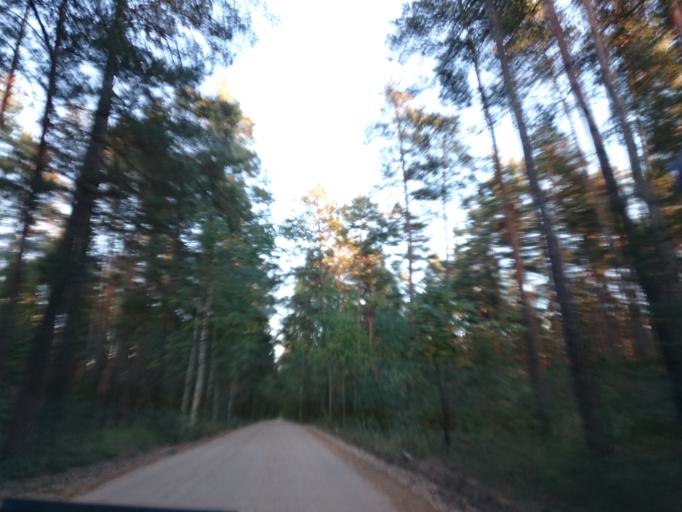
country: LV
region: Adazi
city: Adazi
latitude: 57.0525
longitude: 24.3106
